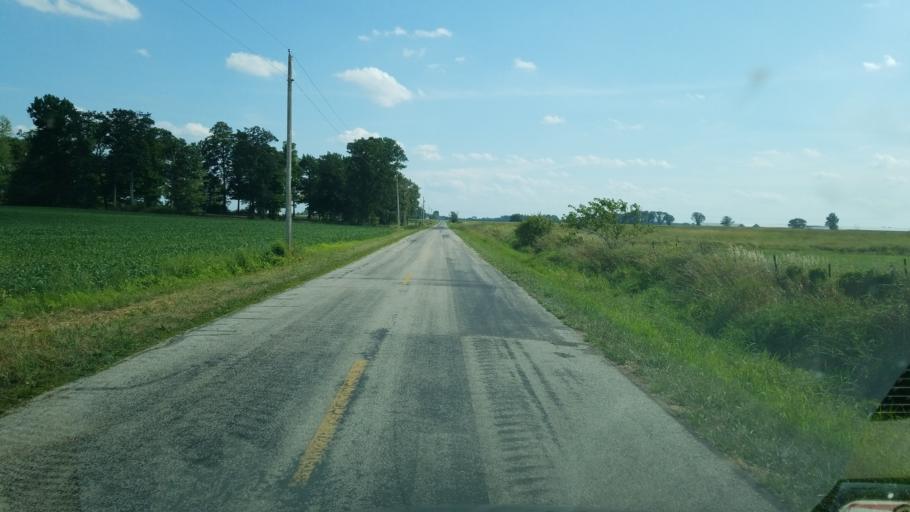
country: US
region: Ohio
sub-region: Union County
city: Richwood
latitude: 40.5468
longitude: -83.3170
